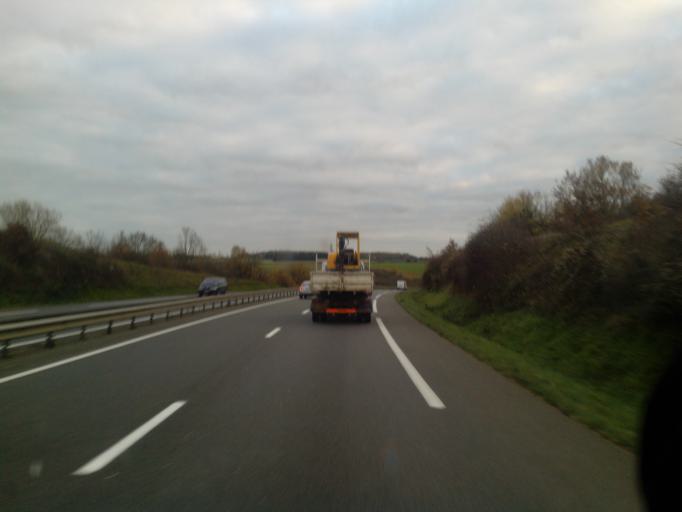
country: FR
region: Poitou-Charentes
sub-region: Departement de la Vienne
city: Montamise
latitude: 46.6073
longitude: 0.3929
